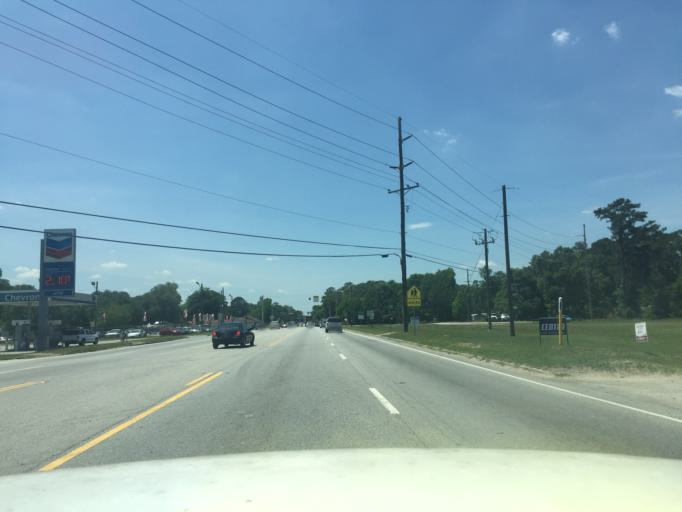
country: US
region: Georgia
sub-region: Chatham County
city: Garden City
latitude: 32.0446
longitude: -81.1810
